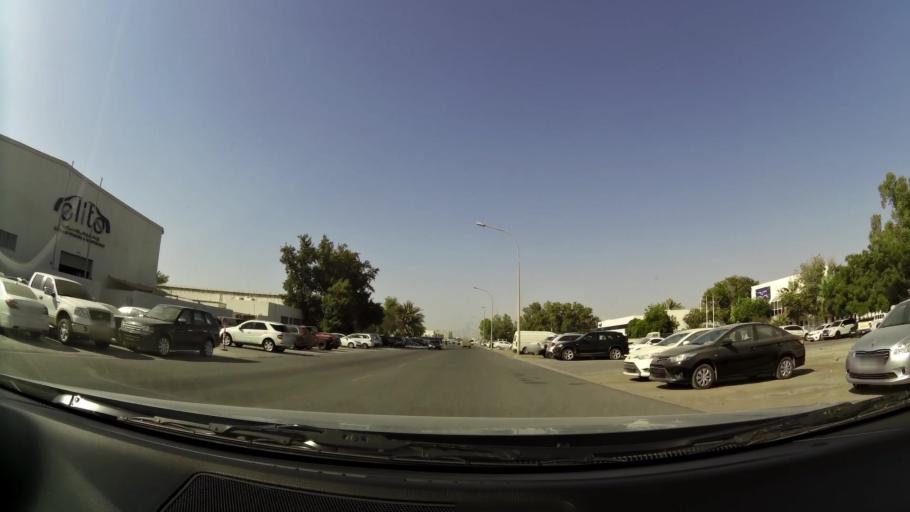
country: AE
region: Dubai
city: Dubai
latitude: 25.1349
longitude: 55.2175
